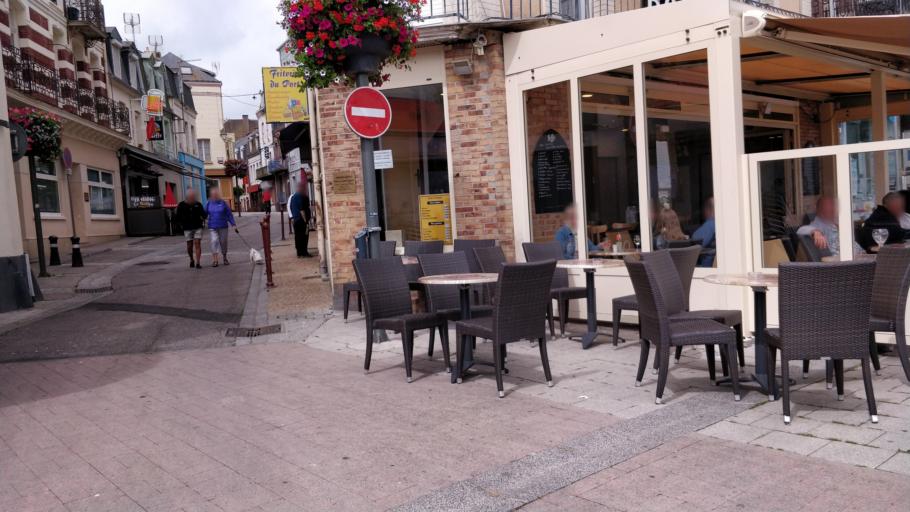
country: FR
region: Haute-Normandie
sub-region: Departement de la Seine-Maritime
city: Le Treport
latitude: 50.0612
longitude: 1.3716
